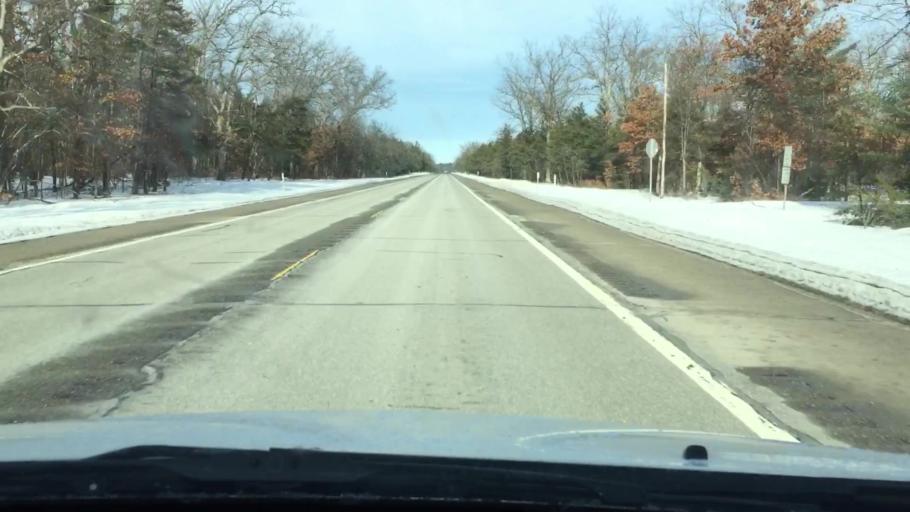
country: US
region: Michigan
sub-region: Wexford County
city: Manton
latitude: 44.5303
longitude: -85.3849
